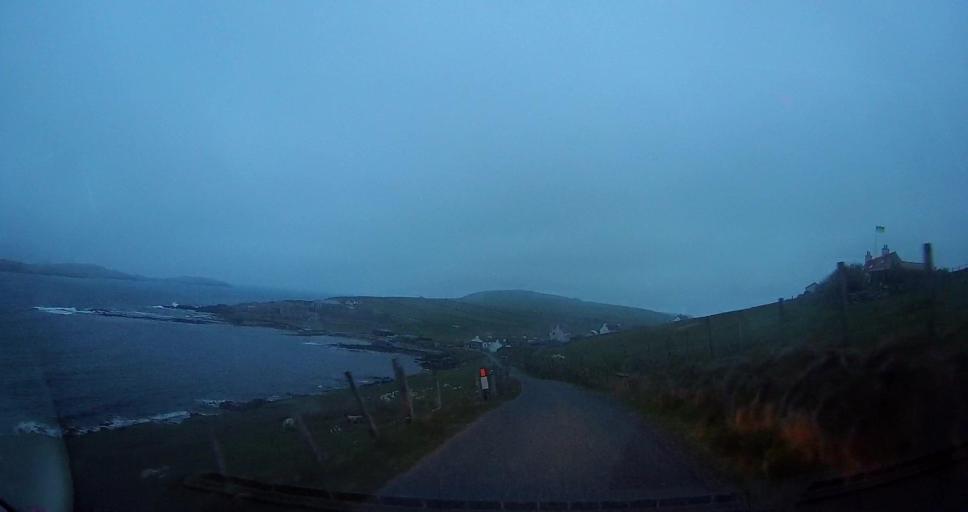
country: GB
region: Scotland
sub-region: Shetland Islands
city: Sandwick
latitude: 60.0096
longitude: -1.2258
